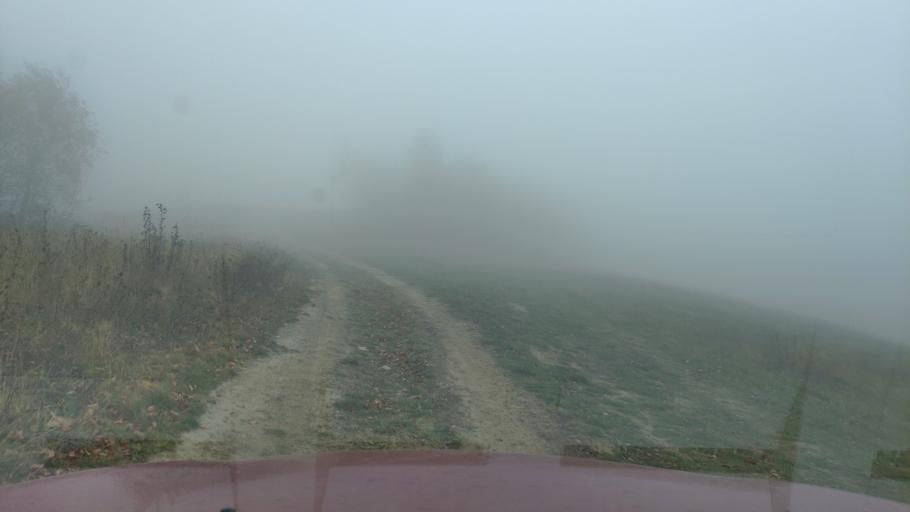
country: SK
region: Presovsky
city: Sabinov
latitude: 49.1501
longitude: 21.2187
